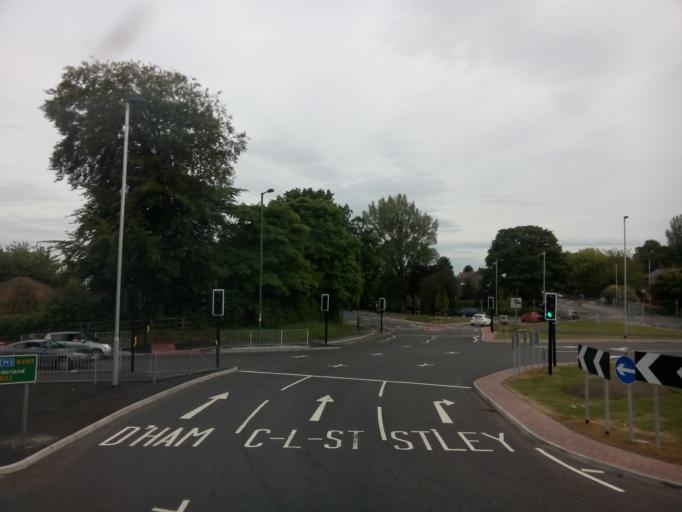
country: GB
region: England
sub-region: County Durham
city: Chester-le-Street
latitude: 54.8682
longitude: -1.5744
